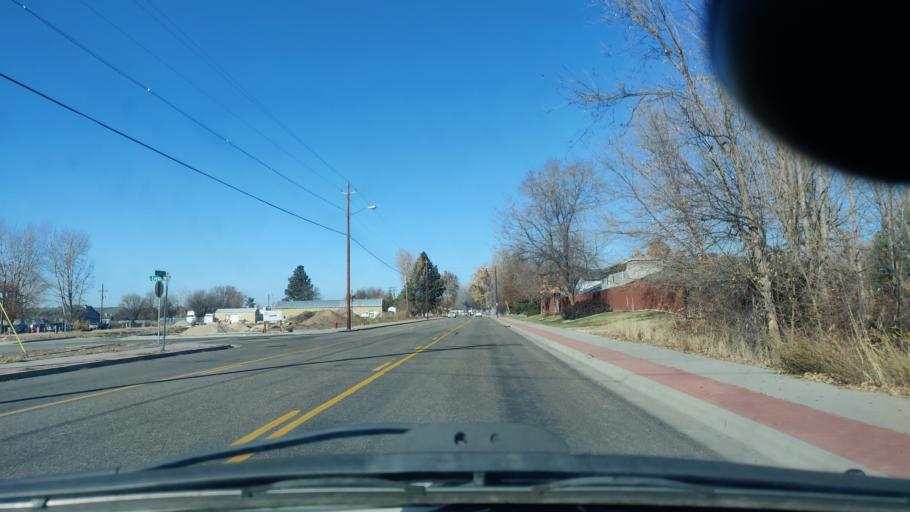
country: US
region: Idaho
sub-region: Ada County
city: Garden City
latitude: 43.6429
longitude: -116.2589
